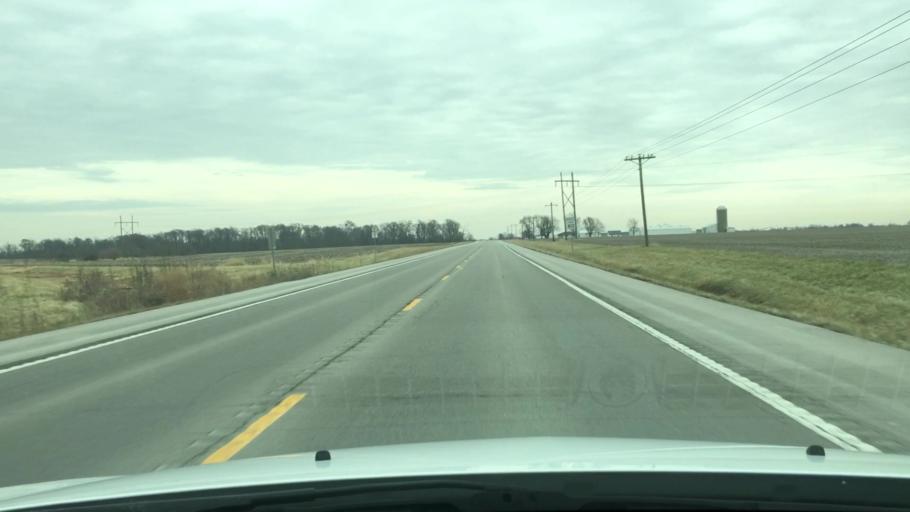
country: US
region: Missouri
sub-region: Audrain County
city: Mexico
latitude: 39.1638
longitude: -91.7591
